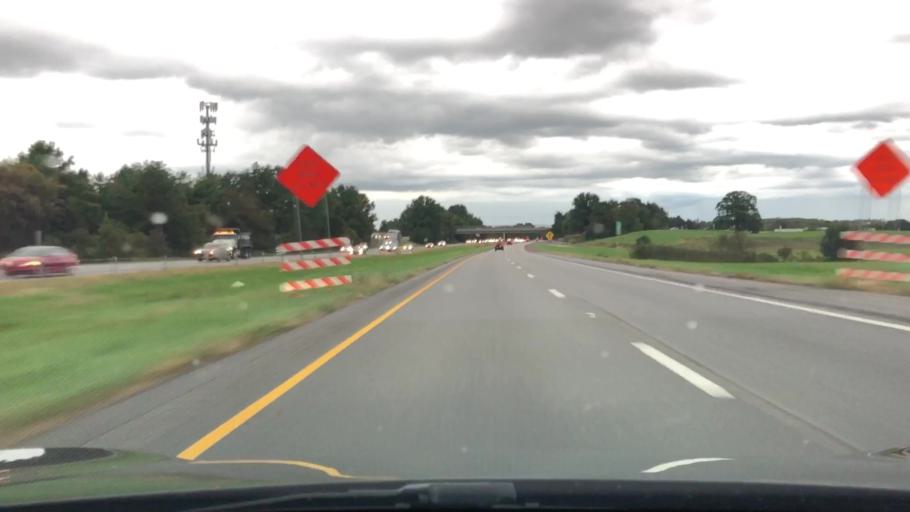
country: US
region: Pennsylvania
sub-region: Bucks County
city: Woodside
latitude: 40.2301
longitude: -74.8820
